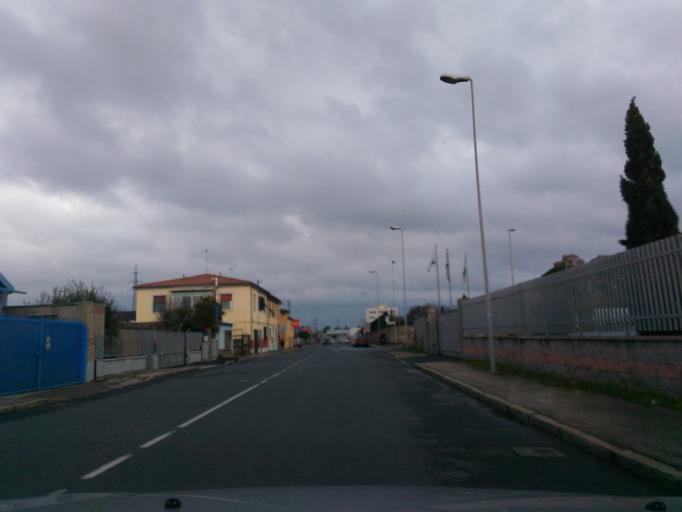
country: IT
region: Tuscany
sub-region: Provincia di Livorno
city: Livorno
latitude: 43.5747
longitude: 10.3385
